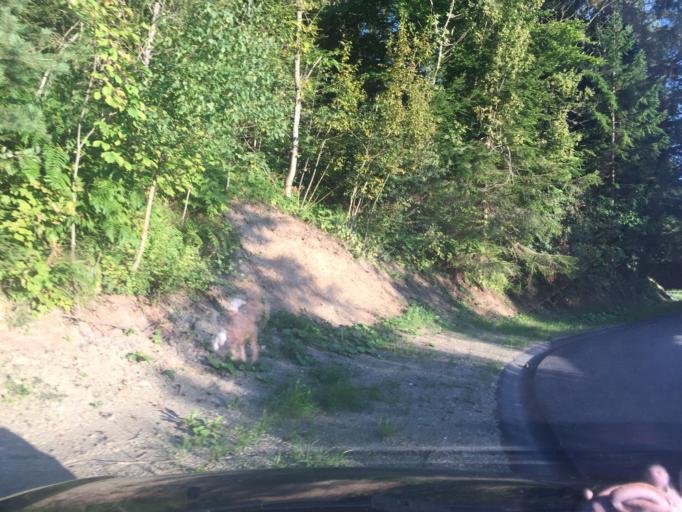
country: SI
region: Sostanj
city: Topolsica
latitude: 46.4517
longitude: 14.9962
